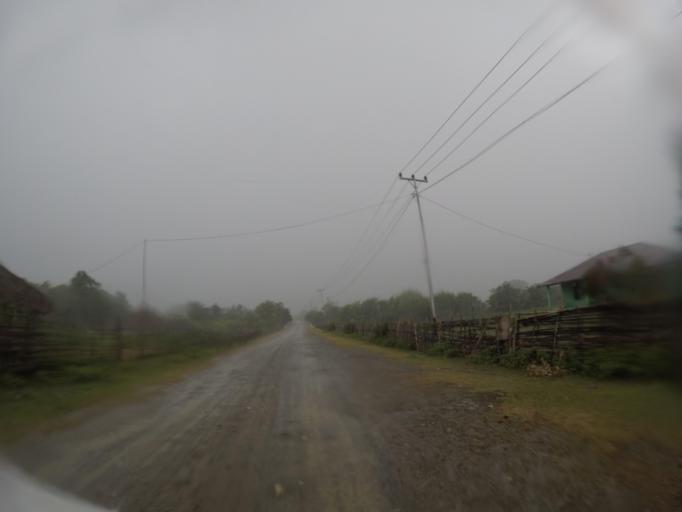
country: TL
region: Bobonaro
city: Maliana
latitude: -8.8560
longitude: 125.1004
